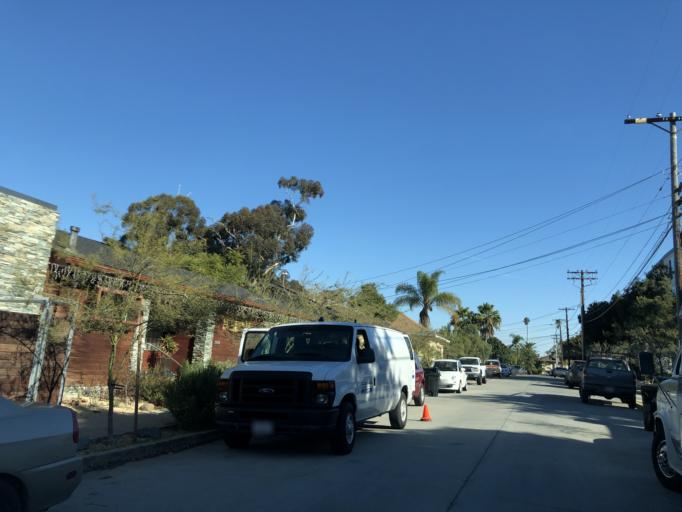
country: US
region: California
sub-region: San Diego County
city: San Diego
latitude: 32.7318
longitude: -117.1316
